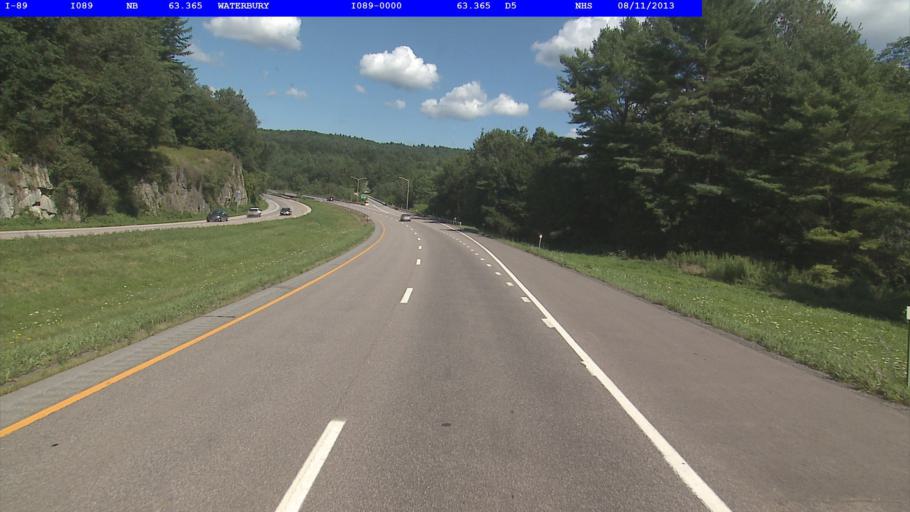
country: US
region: Vermont
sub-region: Washington County
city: Waterbury
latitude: 44.3389
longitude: -72.7470
